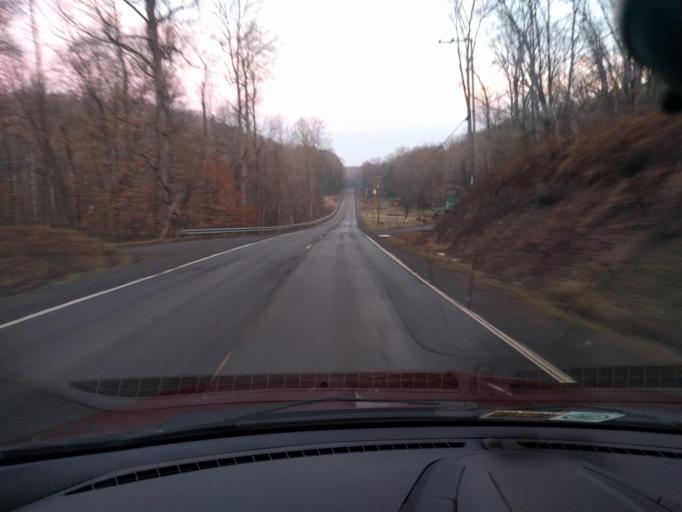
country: US
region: West Virginia
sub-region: Greenbrier County
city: Rainelle
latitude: 38.0291
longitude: -80.9154
